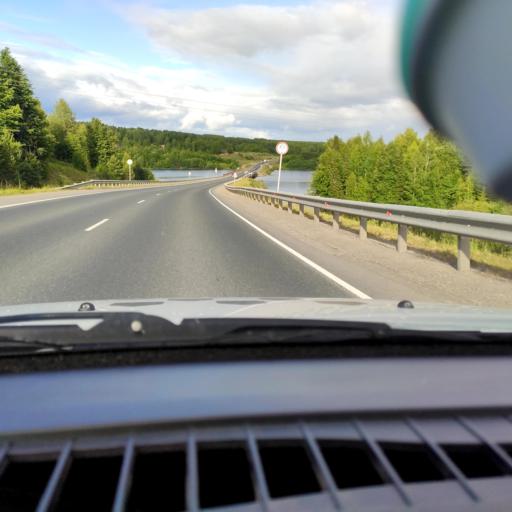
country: RU
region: Perm
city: Sylva
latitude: 58.2953
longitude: 56.8477
